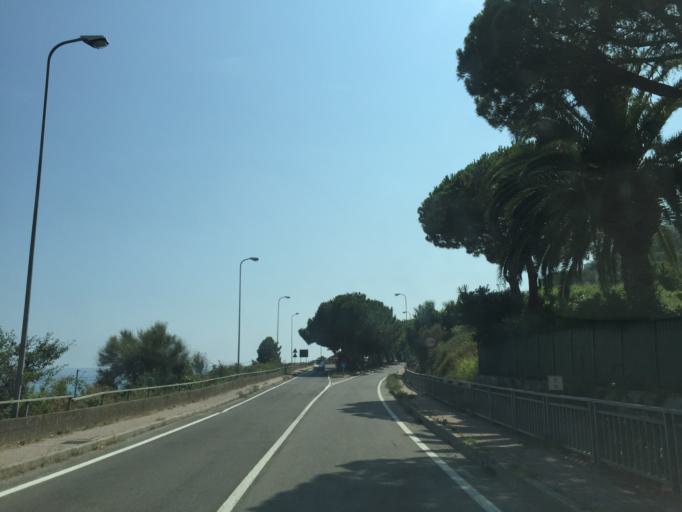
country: IT
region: Liguria
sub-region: Provincia di Imperia
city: Ventimiglia
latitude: 43.7915
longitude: 7.5623
